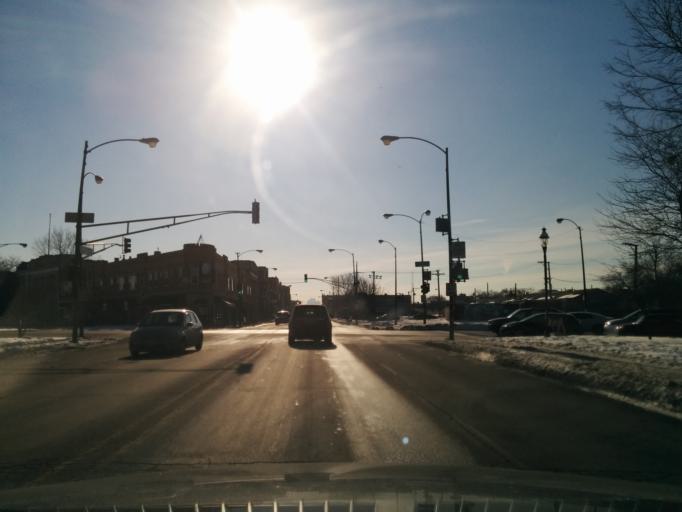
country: US
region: Illinois
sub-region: Cook County
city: Lincolnwood
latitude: 41.9283
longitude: -87.7062
